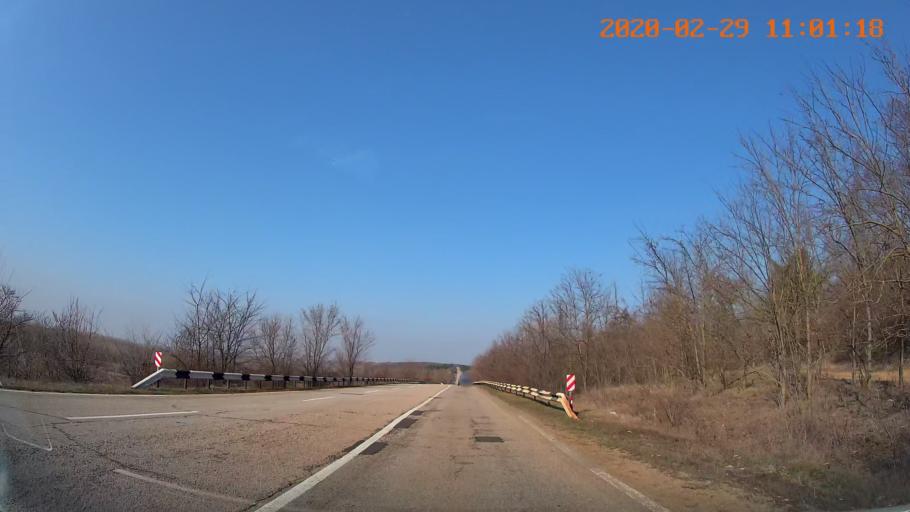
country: MD
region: Telenesti
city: Grigoriopol
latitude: 47.1630
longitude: 29.2609
